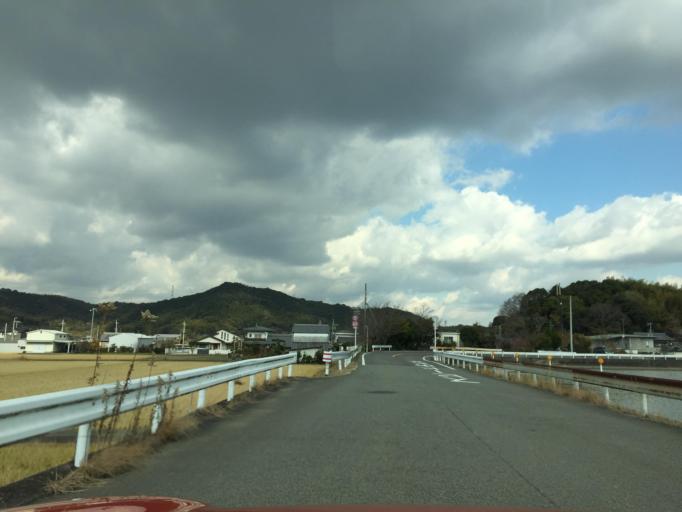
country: JP
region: Wakayama
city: Kainan
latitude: 34.1704
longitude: 135.2244
